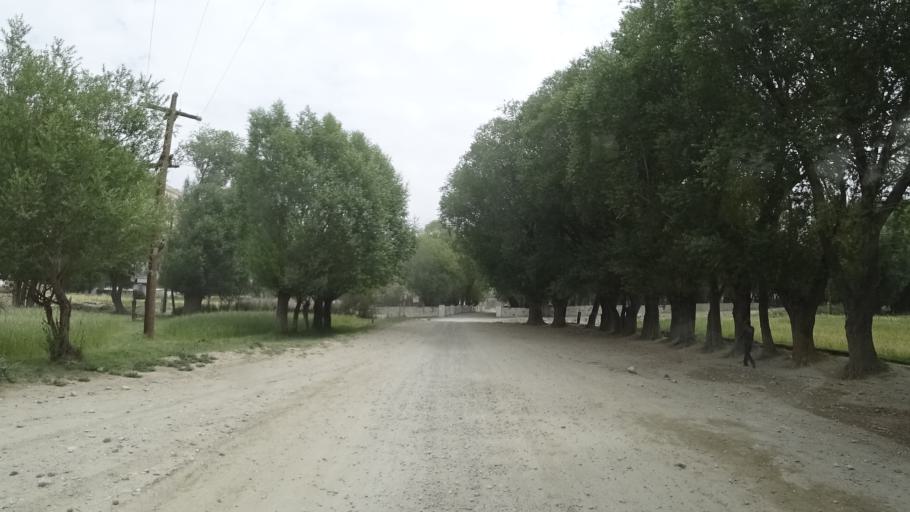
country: AF
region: Badakhshan
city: Khandud
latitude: 37.0375
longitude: 72.6482
